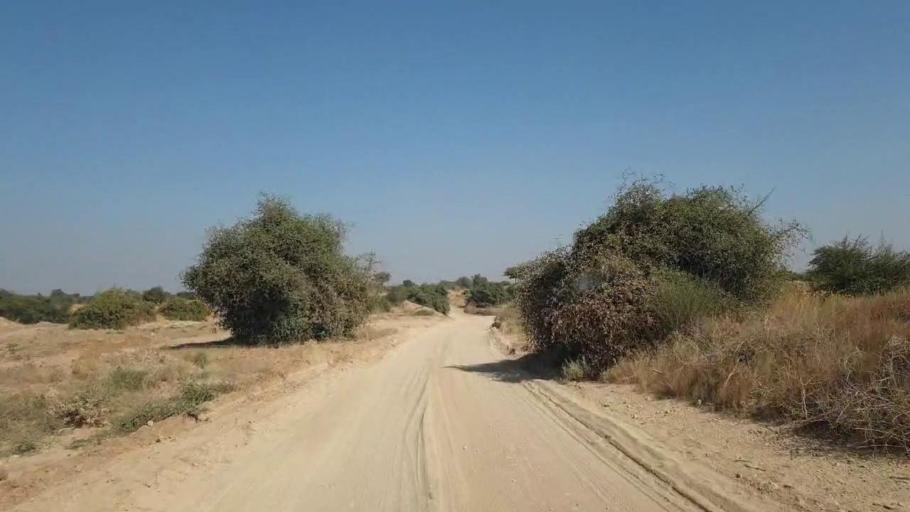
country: PK
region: Sindh
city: Jamshoro
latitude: 25.2811
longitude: 67.8082
